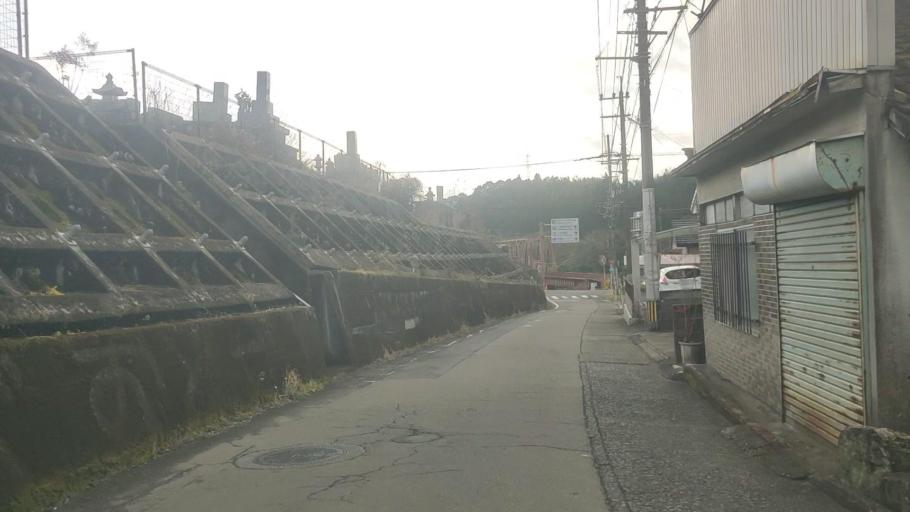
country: JP
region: Kumamoto
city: Hitoyoshi
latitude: 32.2168
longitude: 130.7719
